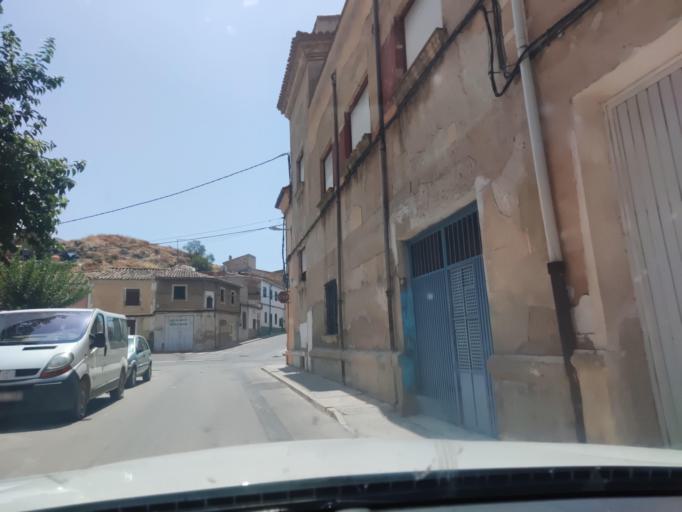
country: ES
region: Castille-La Mancha
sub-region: Provincia de Albacete
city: Hellin
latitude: 38.5165
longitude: -1.6983
